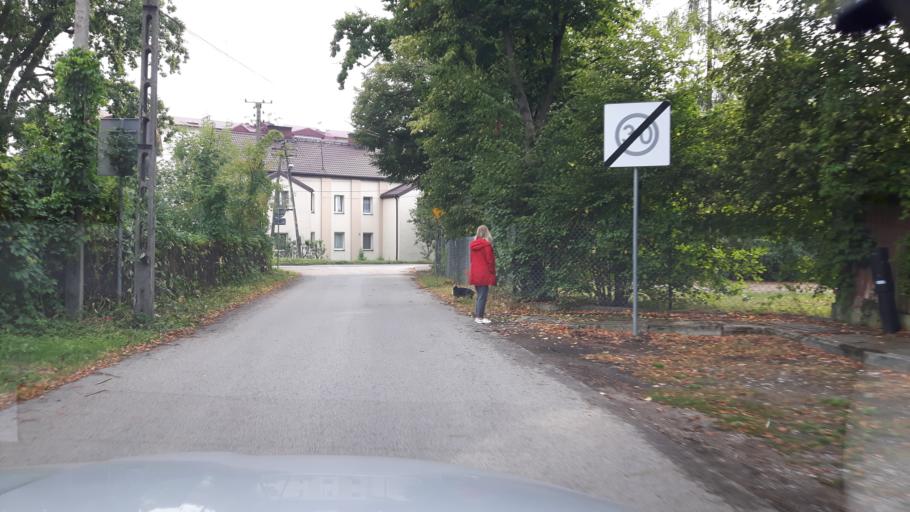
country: PL
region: Masovian Voivodeship
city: Zielonka
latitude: 52.3153
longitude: 21.1549
